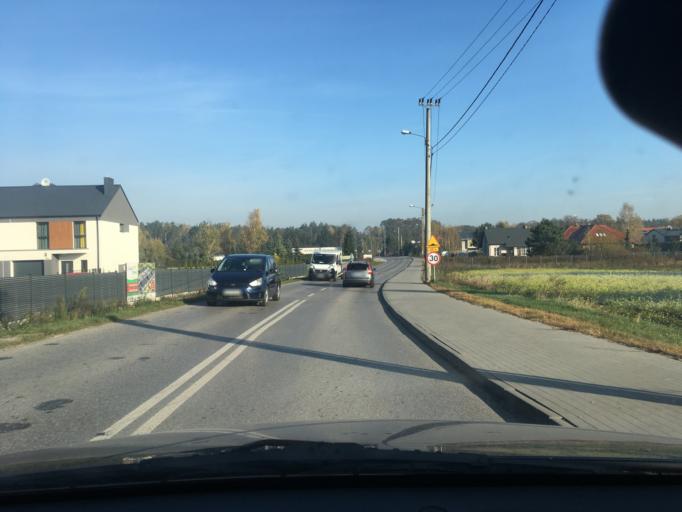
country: PL
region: Masovian Voivodeship
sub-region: Powiat piaseczynski
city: Lesznowola
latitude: 52.0737
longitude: 20.9356
